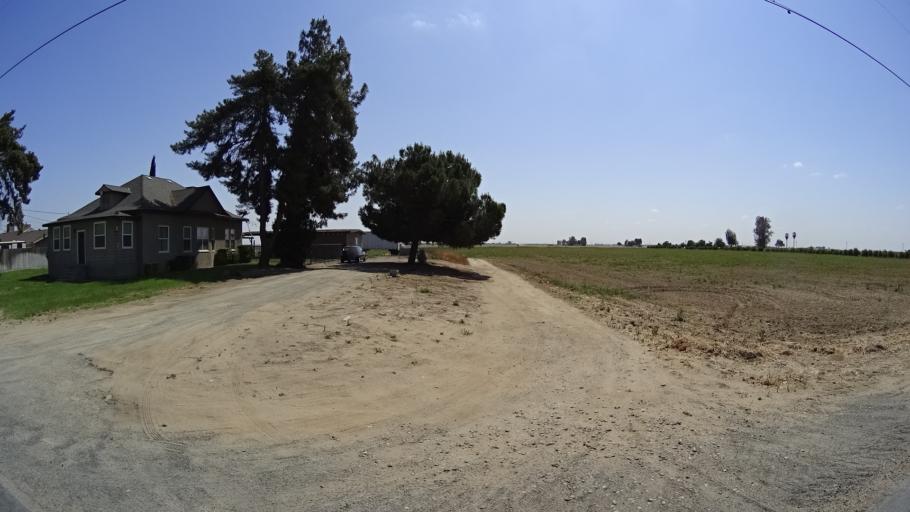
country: US
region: California
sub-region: Kings County
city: Home Garden
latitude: 36.2726
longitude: -119.6190
